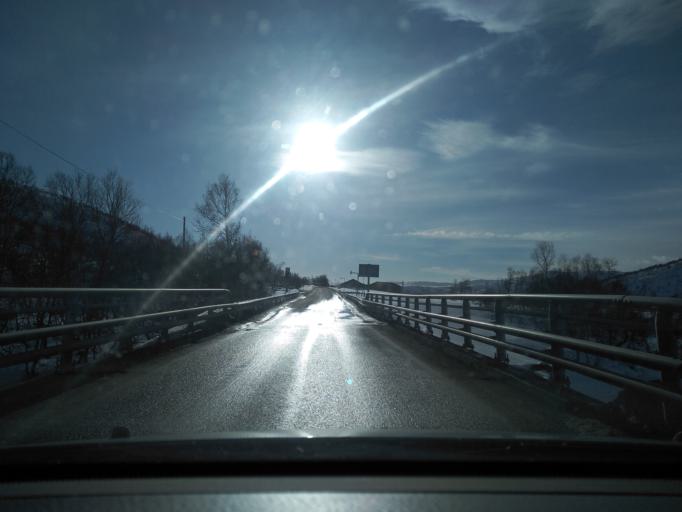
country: NO
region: Aust-Agder
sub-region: Bykle
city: Hovden
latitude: 59.6455
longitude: 7.4620
